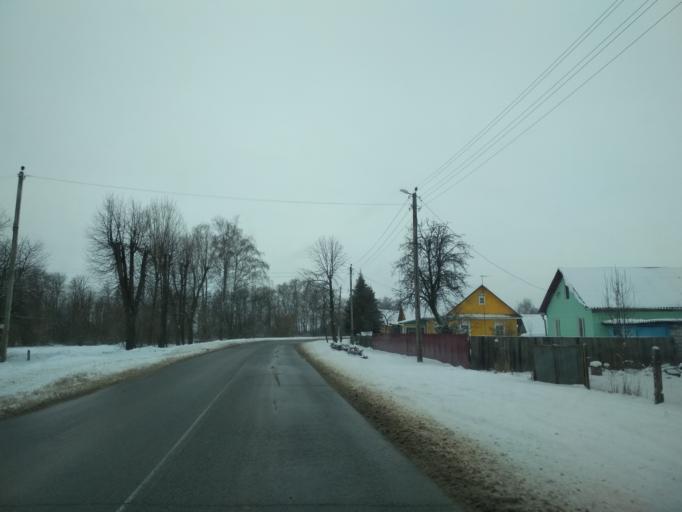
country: BY
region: Minsk
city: Mar''ina Horka
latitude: 53.5260
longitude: 28.1357
